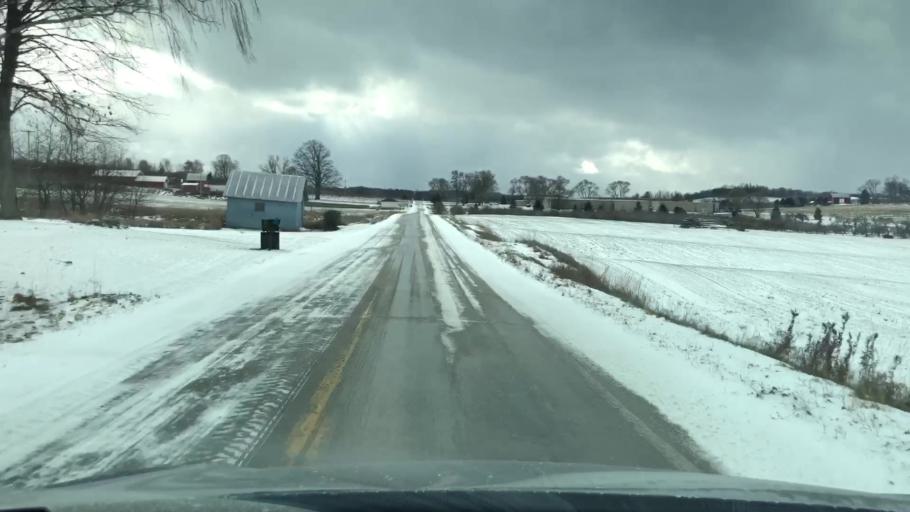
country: US
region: Michigan
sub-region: Antrim County
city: Elk Rapids
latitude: 44.9262
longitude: -85.5156
